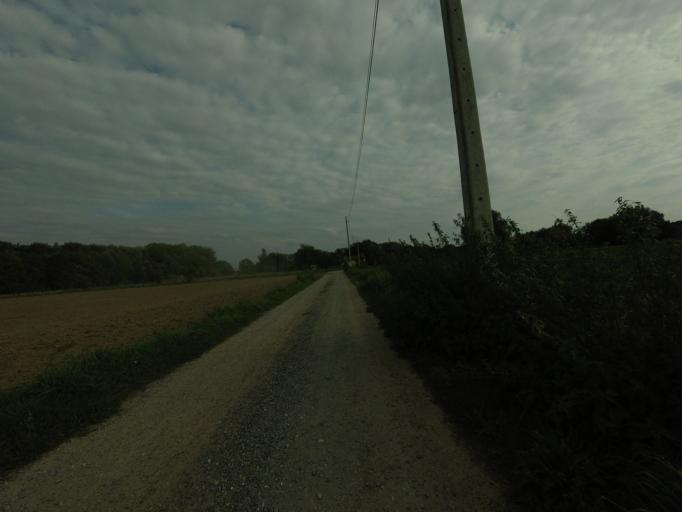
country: BE
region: Flanders
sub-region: Provincie Vlaams-Brabant
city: Kampenhout
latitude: 50.9468
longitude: 4.5262
